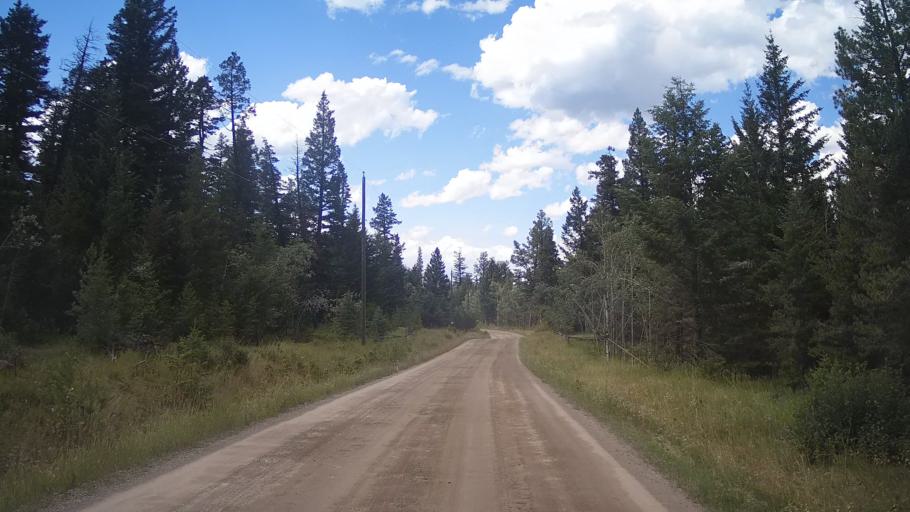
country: CA
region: British Columbia
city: Lillooet
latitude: 51.3075
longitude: -121.8184
